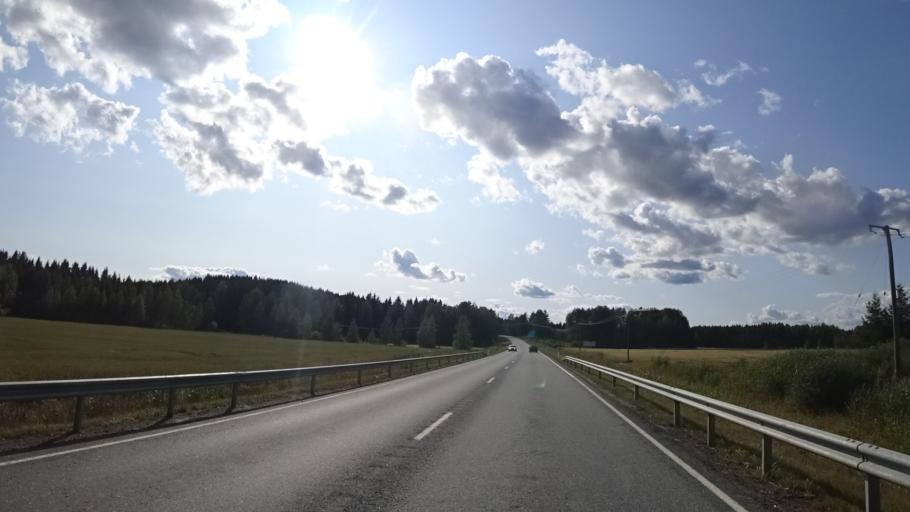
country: FI
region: North Karelia
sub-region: Keski-Karjala
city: Kitee
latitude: 62.0902
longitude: 30.0209
